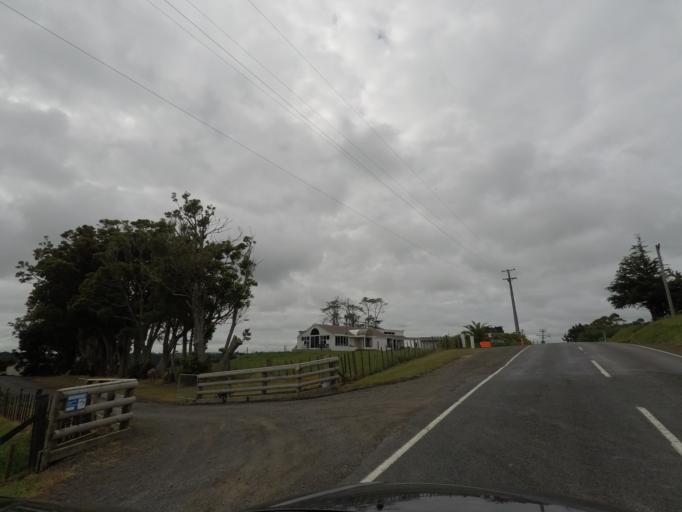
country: NZ
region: Auckland
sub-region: Auckland
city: Rosebank
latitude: -36.8030
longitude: 174.5742
